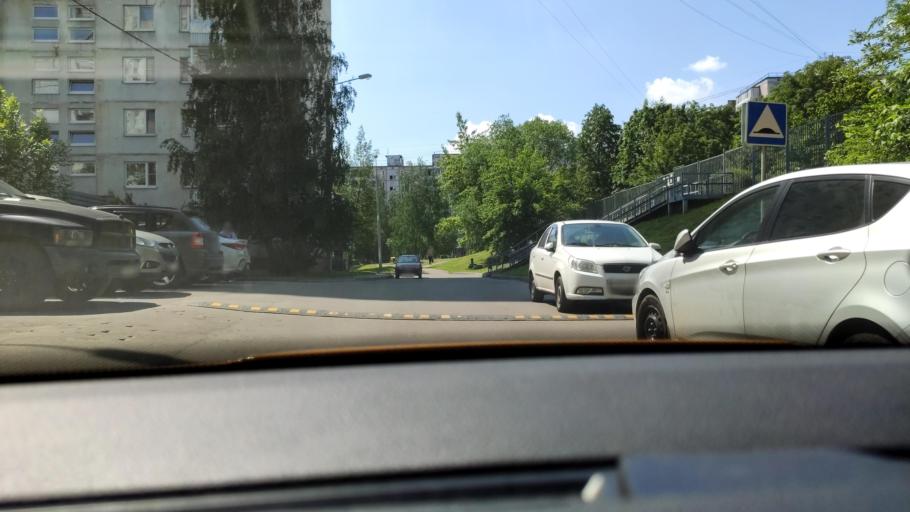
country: RU
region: Moscow
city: Yasenevo
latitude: 55.6058
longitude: 37.5551
